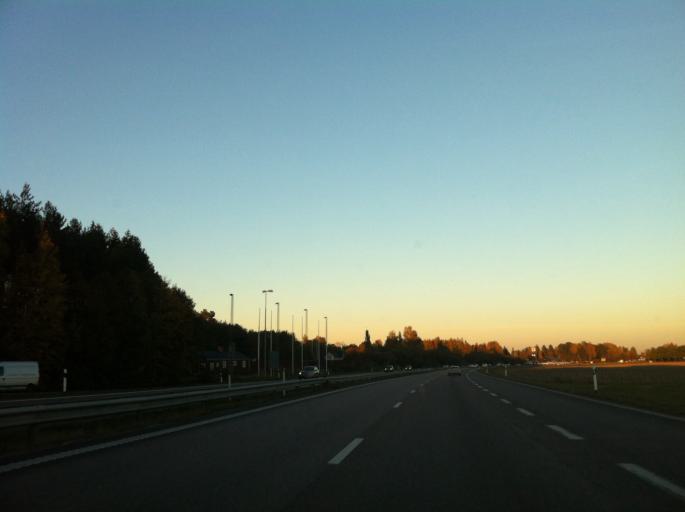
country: SE
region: Gaevleborg
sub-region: Gavle Kommun
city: Valbo
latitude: 60.6468
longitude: 17.0249
